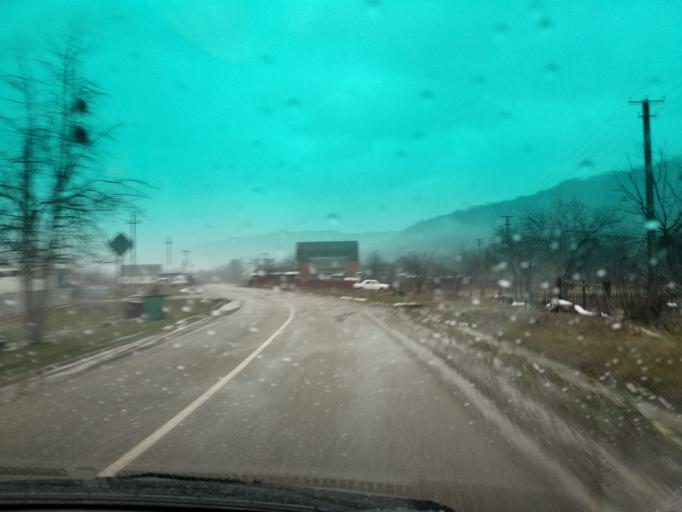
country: RU
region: Krasnodarskiy
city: Khadyzhensk
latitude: 44.2397
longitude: 39.3800
